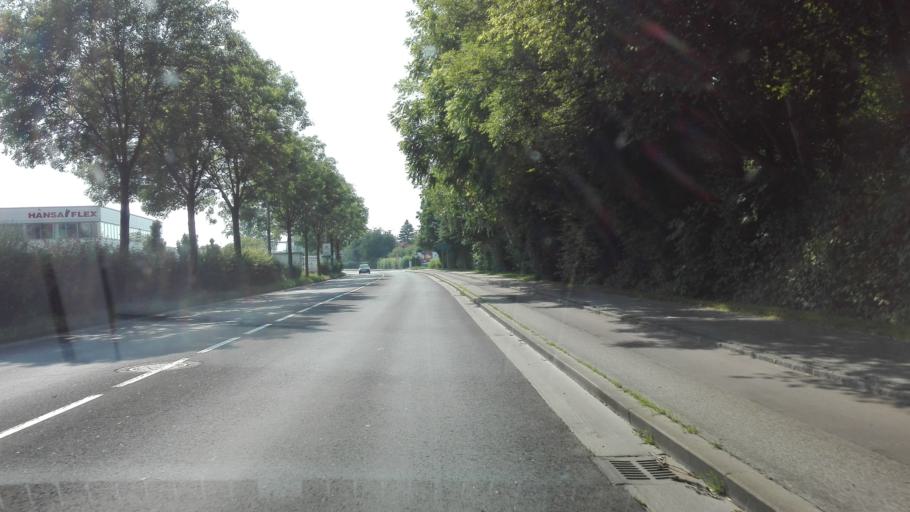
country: AT
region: Upper Austria
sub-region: Politischer Bezirk Linz-Land
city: Ansfelden
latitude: 48.2424
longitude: 14.2905
